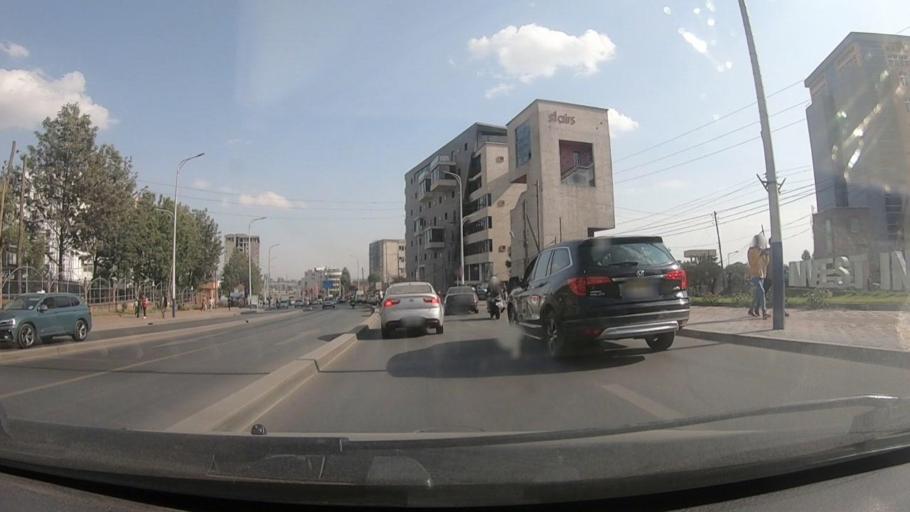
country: ET
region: Adis Abeba
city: Addis Ababa
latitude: 8.9914
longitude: 38.7400
